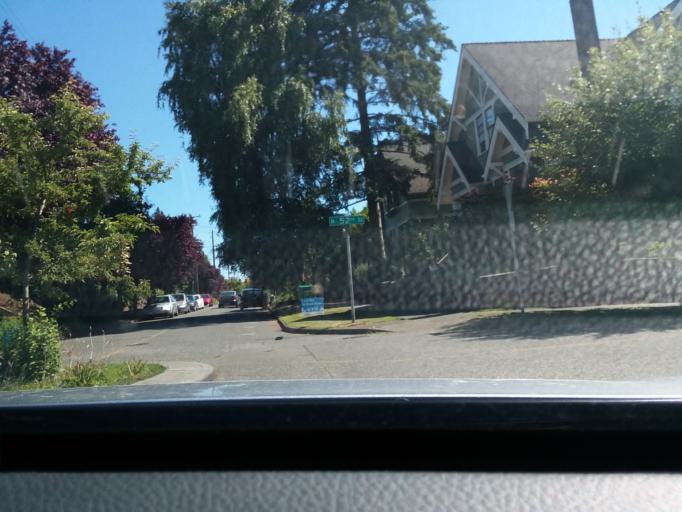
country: US
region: Washington
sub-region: King County
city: Seattle
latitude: 47.6666
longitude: -122.3365
